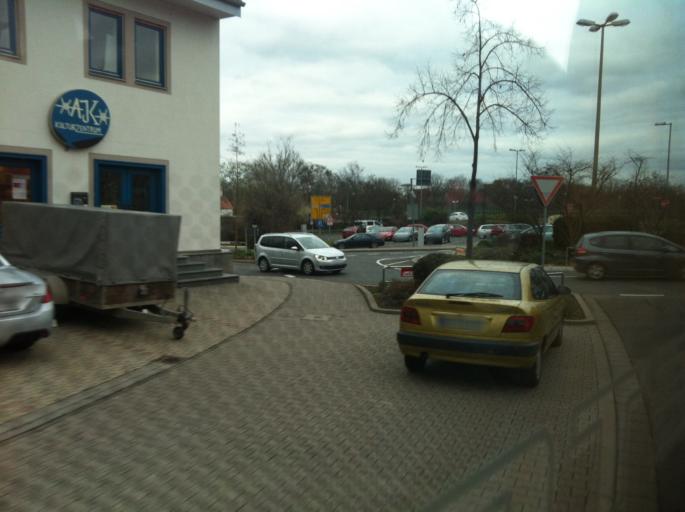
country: DE
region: Rheinland-Pfalz
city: Bad Kreuznach
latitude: 49.8437
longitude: 7.8627
